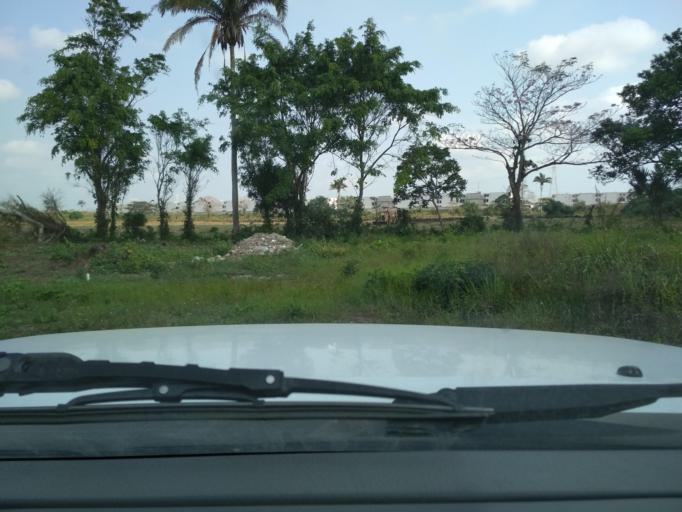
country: MX
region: Veracruz
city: El Tejar
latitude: 19.0852
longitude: -96.1661
